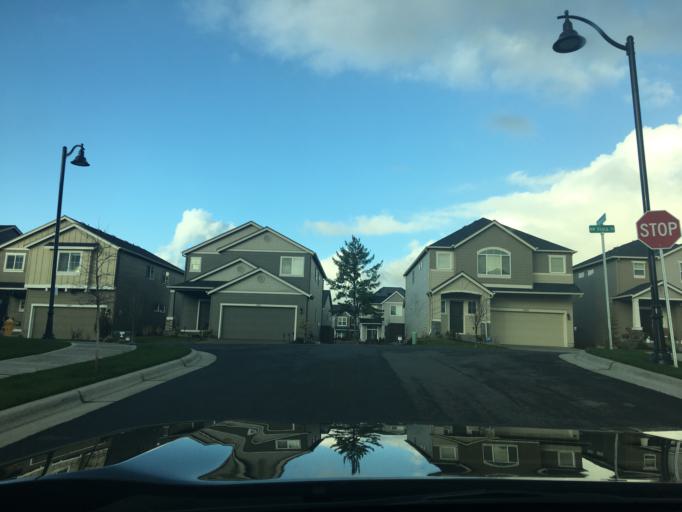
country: US
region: Oregon
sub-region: Washington County
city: Bethany
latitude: 45.5733
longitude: -122.8521
